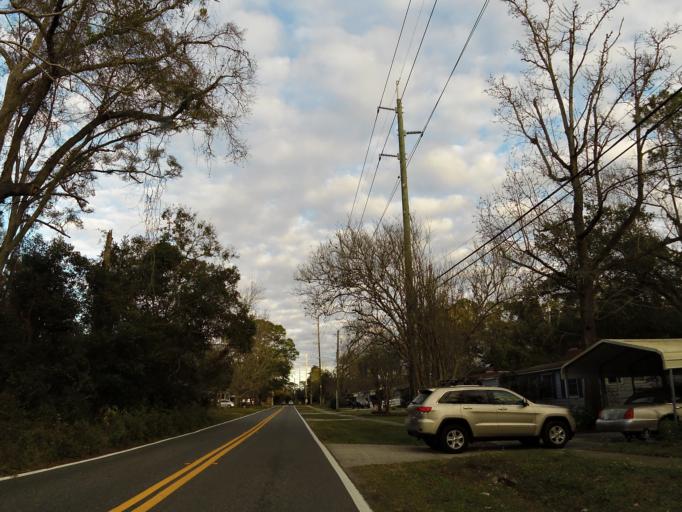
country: US
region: Florida
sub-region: Duval County
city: Jacksonville
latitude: 30.3031
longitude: -81.7242
